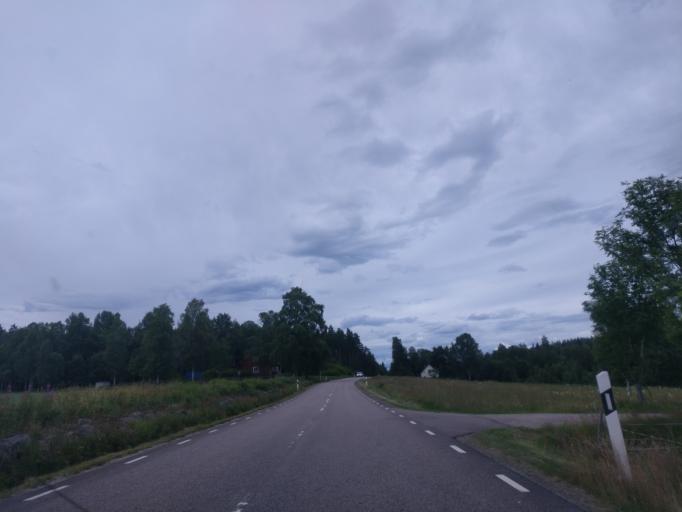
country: SE
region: Vaermland
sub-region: Hagfors Kommun
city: Ekshaerad
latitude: 60.1615
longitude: 13.4742
